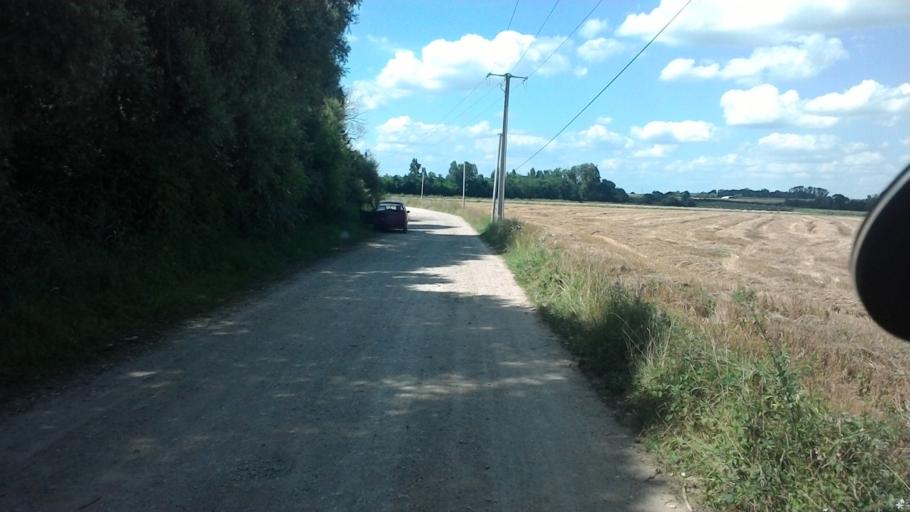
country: FR
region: Bourgogne
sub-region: Departement de la Cote-d'Or
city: Seurre
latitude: 46.9376
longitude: 5.1545
